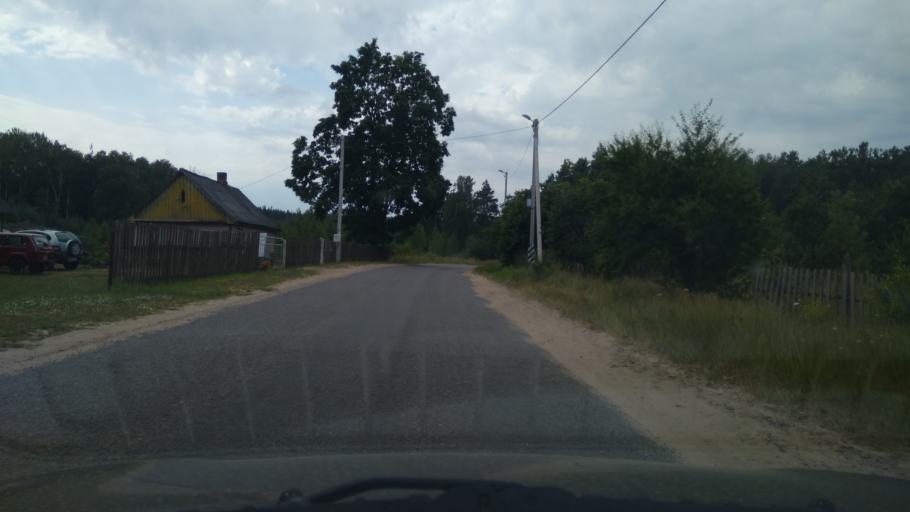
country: BY
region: Brest
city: Nyakhachava
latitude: 52.6083
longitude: 25.0862
